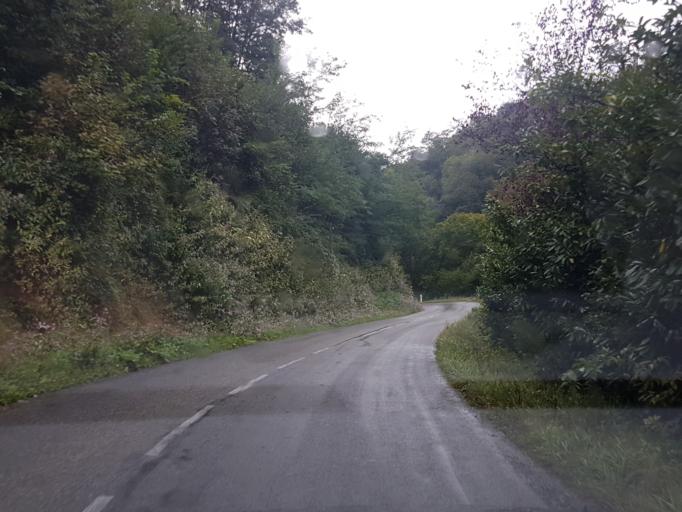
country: FR
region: Midi-Pyrenees
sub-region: Departement de l'Ariege
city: Saint-Girons
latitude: 42.9045
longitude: 1.2443
